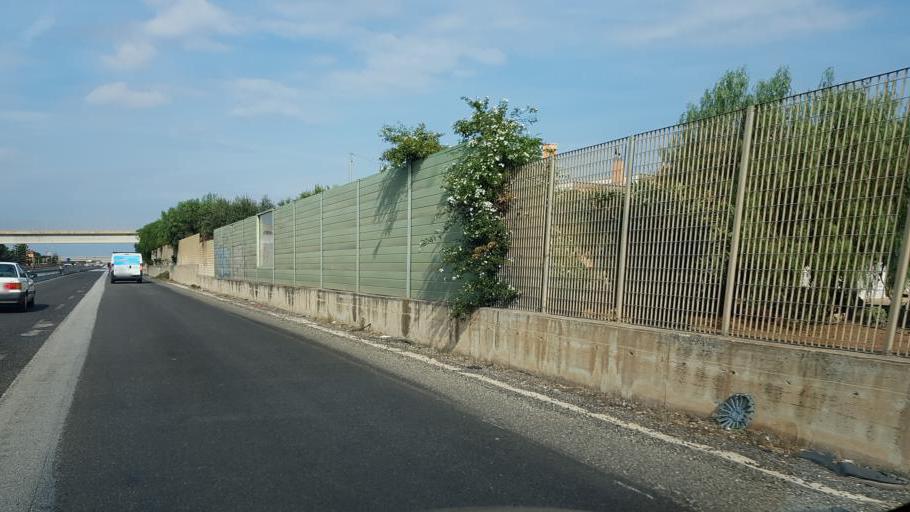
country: IT
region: Apulia
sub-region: Provincia di Brindisi
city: Fasano
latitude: 40.8665
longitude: 17.3455
